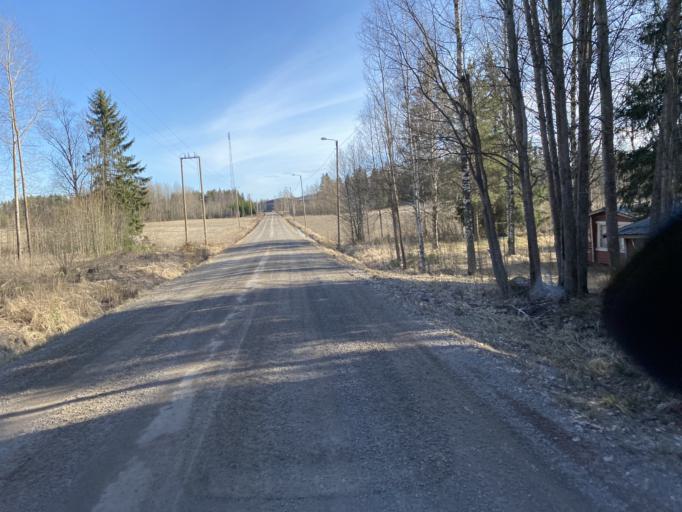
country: FI
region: Satakunta
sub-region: Rauma
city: Lappi
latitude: 61.1324
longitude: 21.9490
